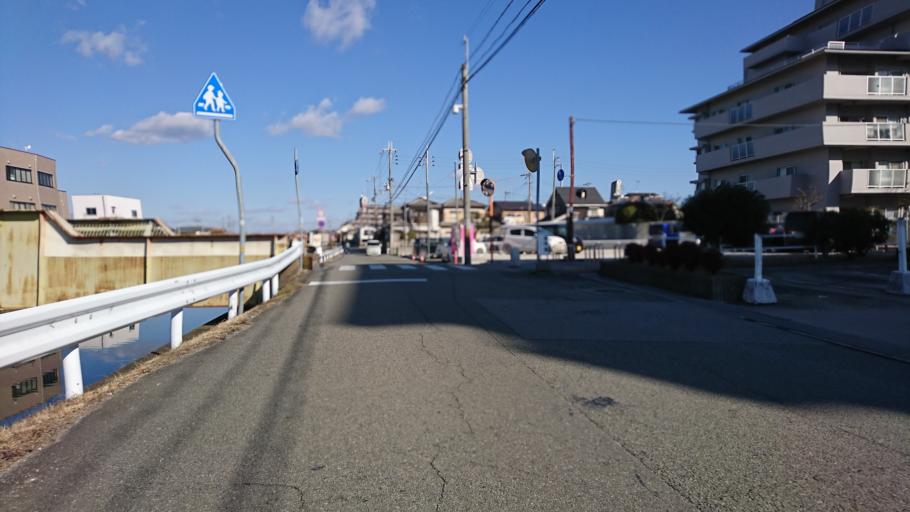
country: JP
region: Hyogo
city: Kakogawacho-honmachi
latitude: 34.7507
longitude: 134.8377
